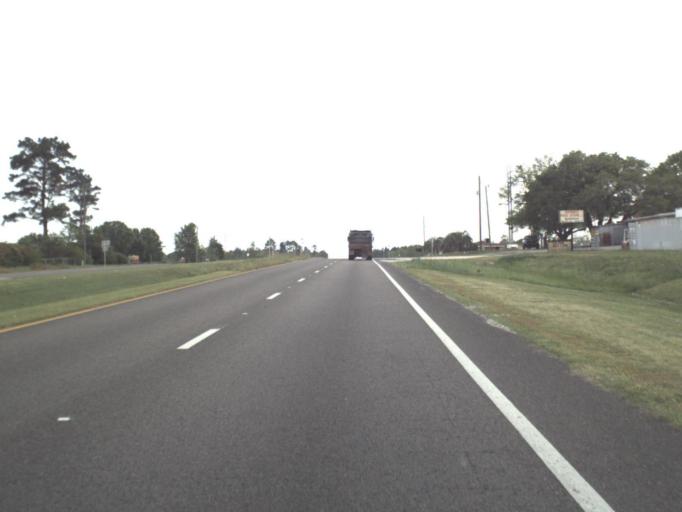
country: US
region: Florida
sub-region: Escambia County
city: Molino
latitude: 30.7036
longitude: -87.3505
